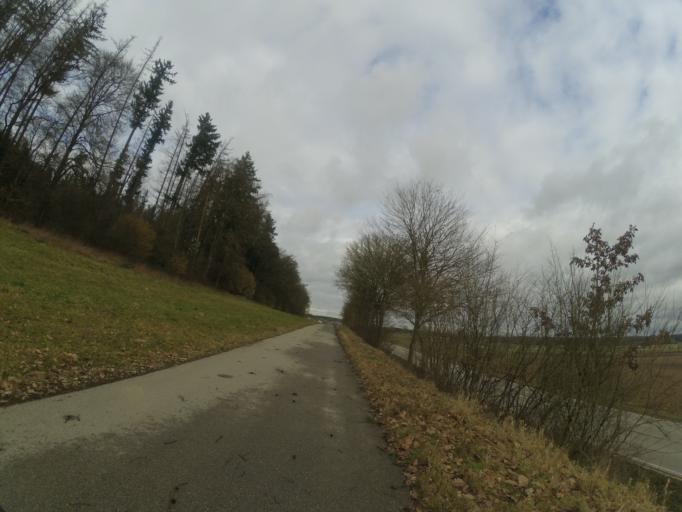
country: DE
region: Bavaria
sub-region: Swabia
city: Bellenberg
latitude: 48.2636
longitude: 10.1259
